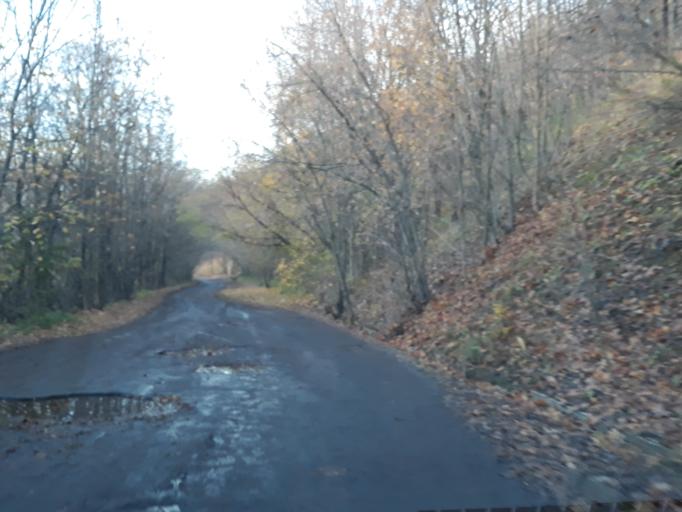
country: RU
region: Nizjnij Novgorod
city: Nizhniy Novgorod
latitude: 56.2859
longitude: 43.9697
